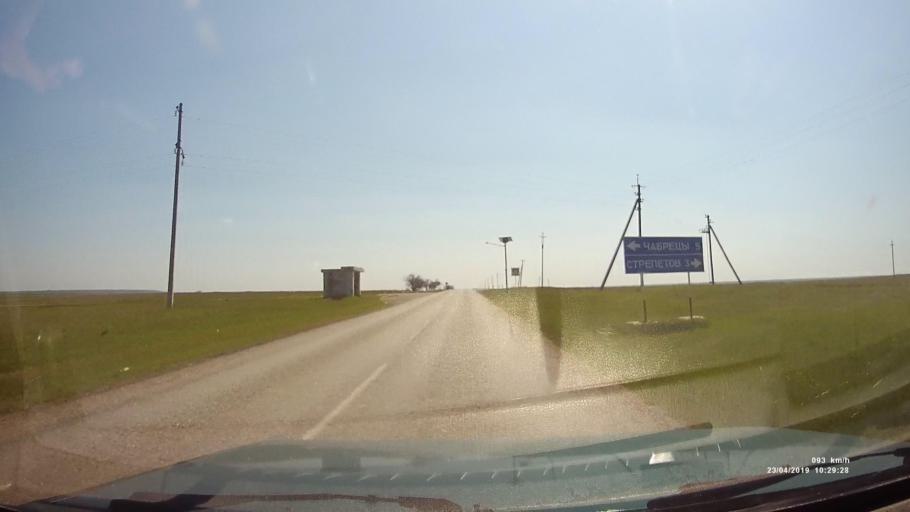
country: RU
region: Kalmykiya
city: Yashalta
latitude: 46.5983
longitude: 42.5270
